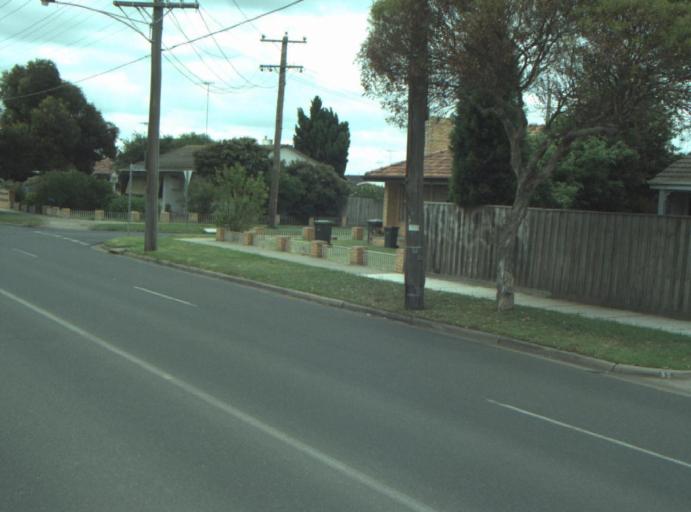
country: AU
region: Victoria
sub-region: Greater Geelong
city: Bell Park
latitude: -38.0745
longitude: 144.3620
